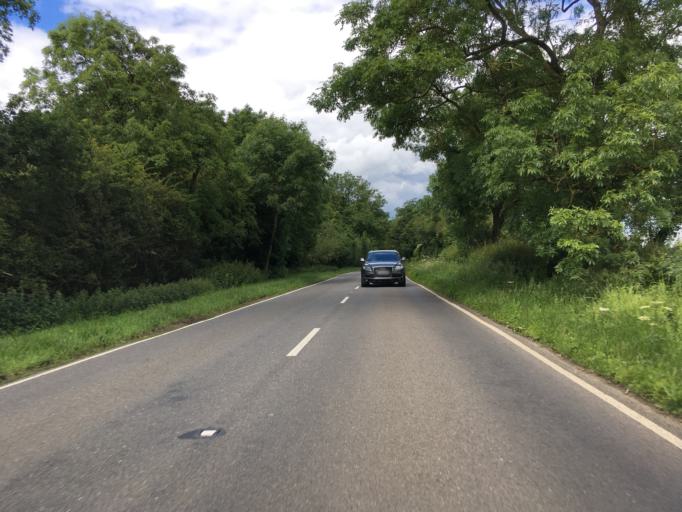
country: GB
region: England
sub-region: Northamptonshire
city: Brackley
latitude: 52.0736
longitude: -1.1162
